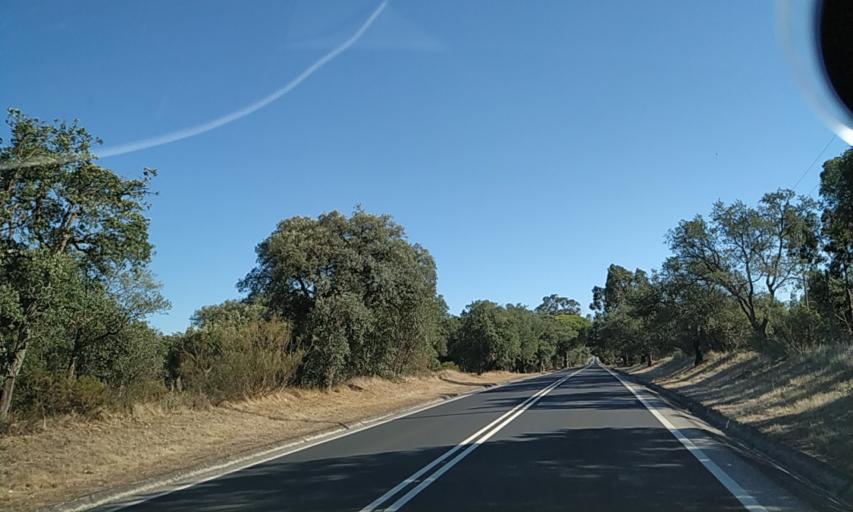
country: PT
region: Santarem
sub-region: Benavente
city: Poceirao
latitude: 38.8398
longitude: -8.8810
